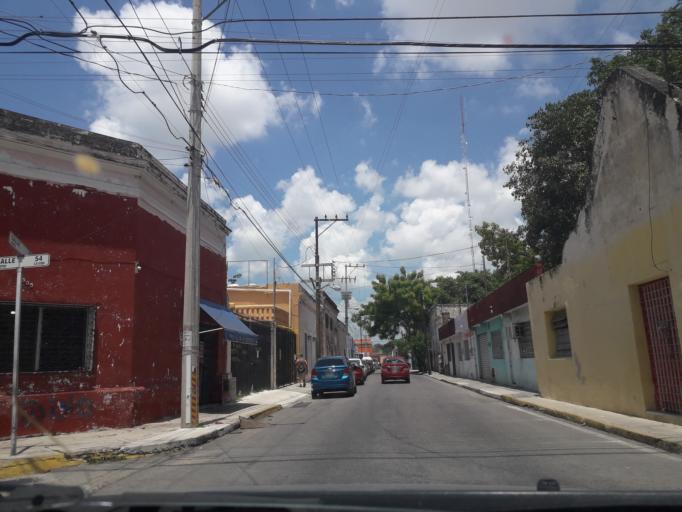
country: MX
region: Yucatan
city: Merida
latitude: 20.9595
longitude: -89.6207
